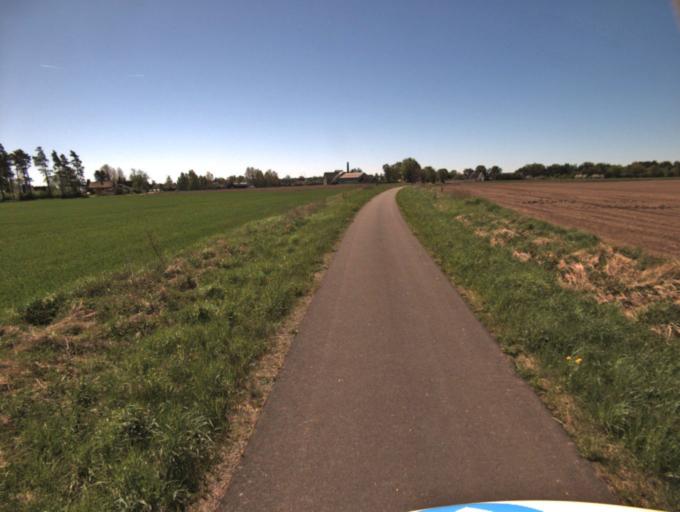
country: SE
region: Skane
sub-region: Kristianstads Kommun
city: Norra Asum
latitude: 55.9540
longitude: 14.1566
